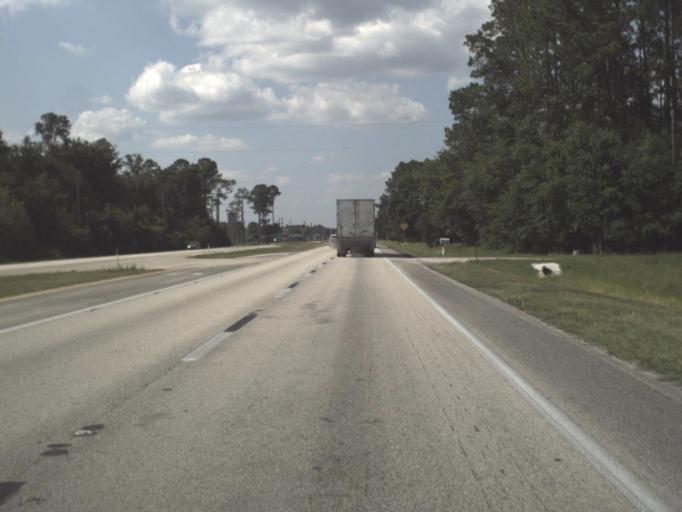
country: US
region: Florida
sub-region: Alachua County
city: Waldo
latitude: 29.8088
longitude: -82.1676
